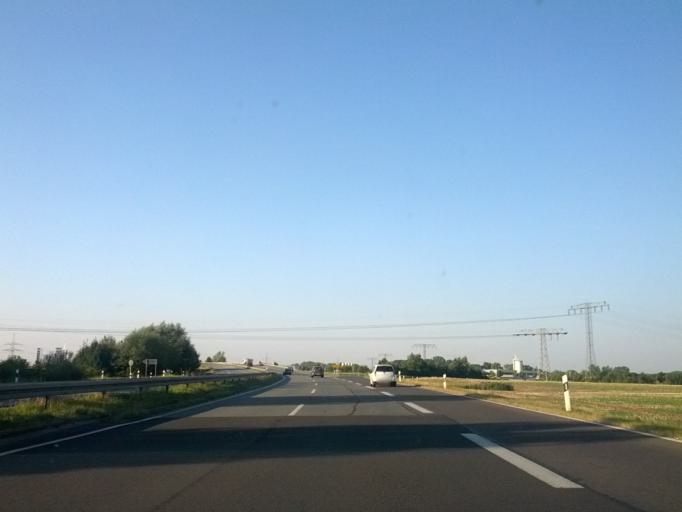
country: DE
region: Mecklenburg-Vorpommern
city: Stralsund
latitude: 54.2887
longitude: 13.0747
